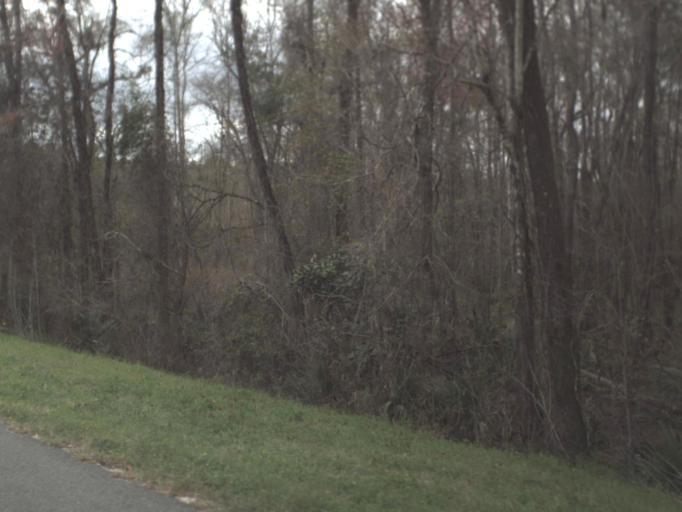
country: US
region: Florida
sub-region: Gadsden County
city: Quincy
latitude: 30.4910
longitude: -84.6158
